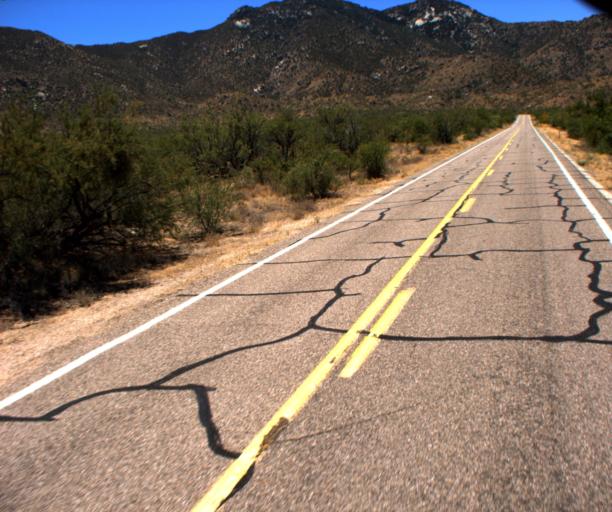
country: US
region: Arizona
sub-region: Pima County
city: Three Points
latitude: 31.9949
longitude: -111.5731
